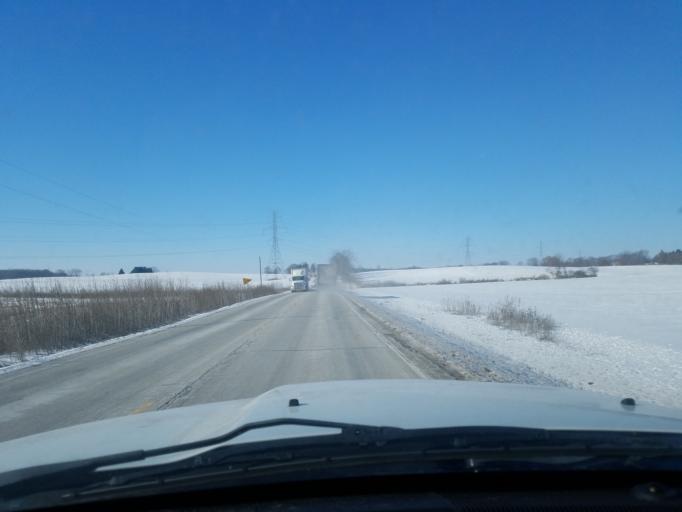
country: US
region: Indiana
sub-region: Noble County
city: Avilla
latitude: 41.3946
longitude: -85.2721
